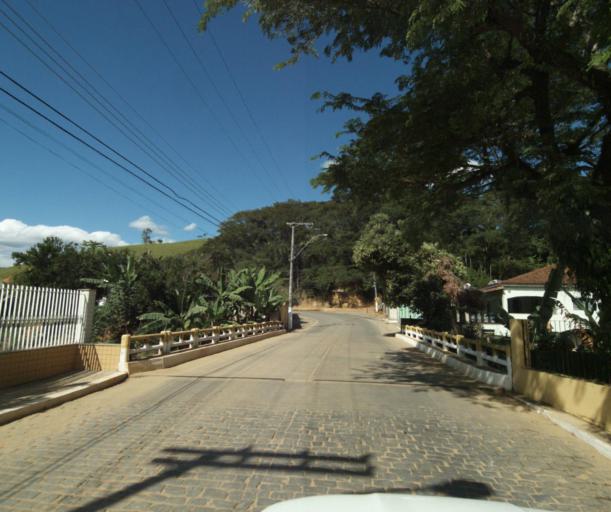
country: BR
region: Espirito Santo
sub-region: Sao Jose Do Calcado
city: Sao Jose do Calcado
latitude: -21.0237
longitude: -41.6509
